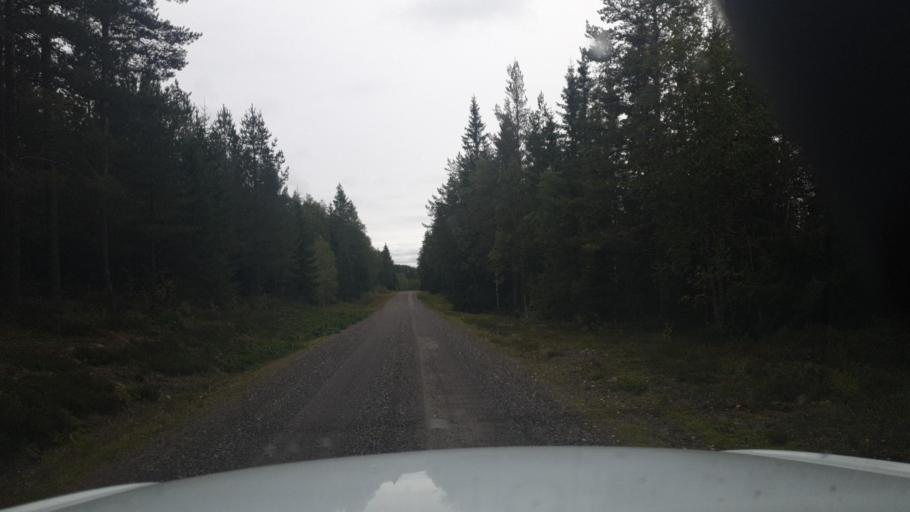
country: SE
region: Vaermland
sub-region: Eda Kommun
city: Charlottenberg
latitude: 60.1191
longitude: 12.6012
